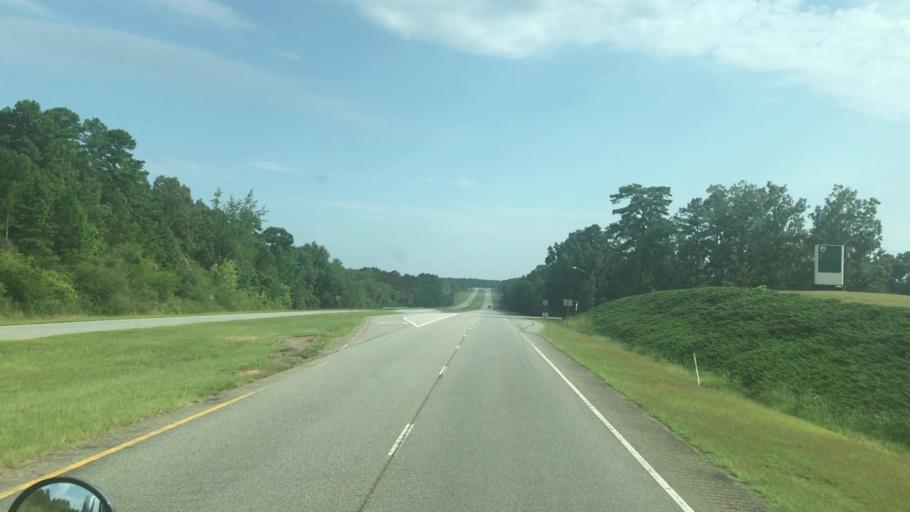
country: US
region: Georgia
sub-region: Early County
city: Blakely
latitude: 31.3955
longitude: -84.9242
